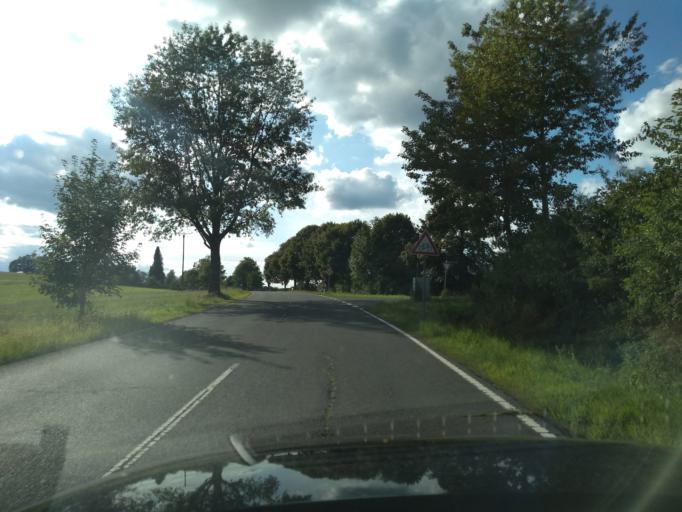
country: DE
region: North Rhine-Westphalia
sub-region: Regierungsbezirk Koln
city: Much
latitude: 50.8486
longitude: 7.3929
